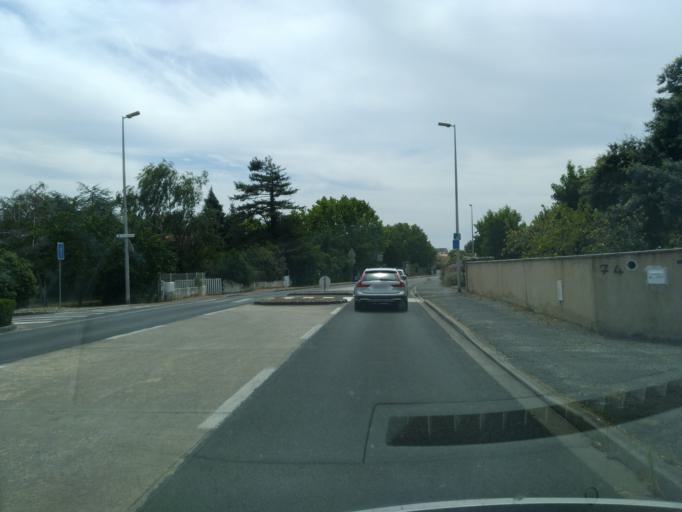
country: FR
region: Poitou-Charentes
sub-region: Departement de la Charente-Maritime
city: Saint-Palais-sur-Mer
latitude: 45.6493
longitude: -1.0815
